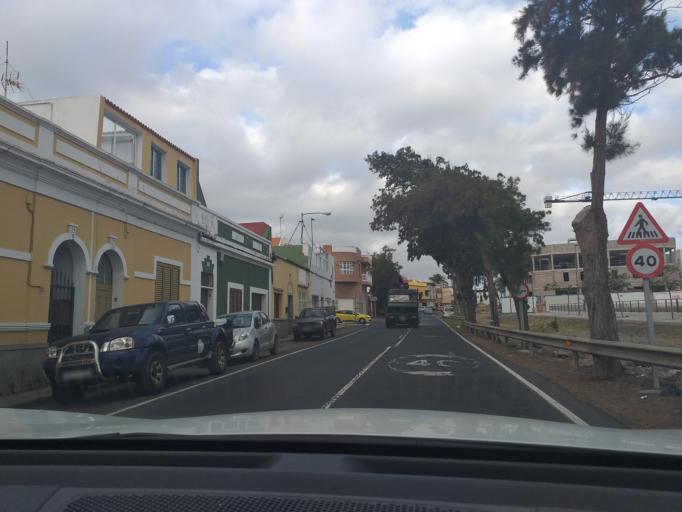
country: ES
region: Canary Islands
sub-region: Provincia de Las Palmas
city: Arucas
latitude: 28.0986
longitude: -15.4807
